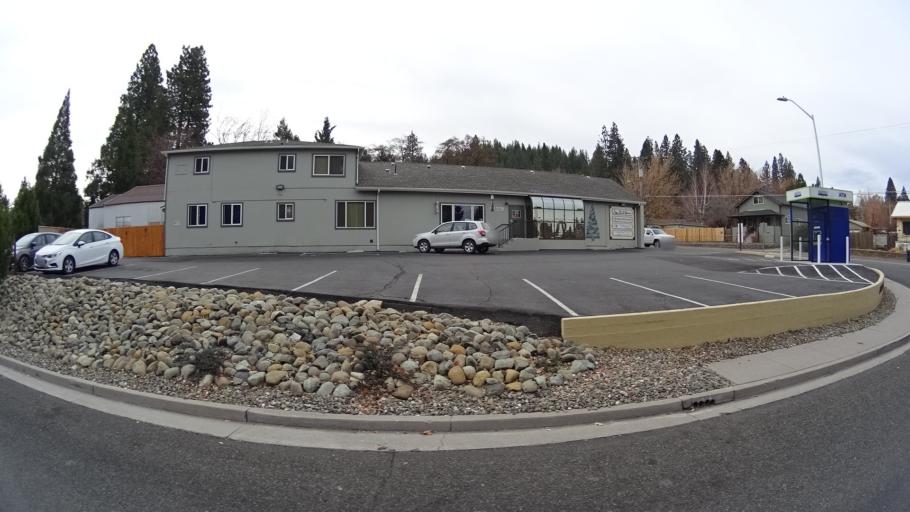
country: US
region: California
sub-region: Siskiyou County
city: Weed
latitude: 41.4141
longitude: -122.3831
